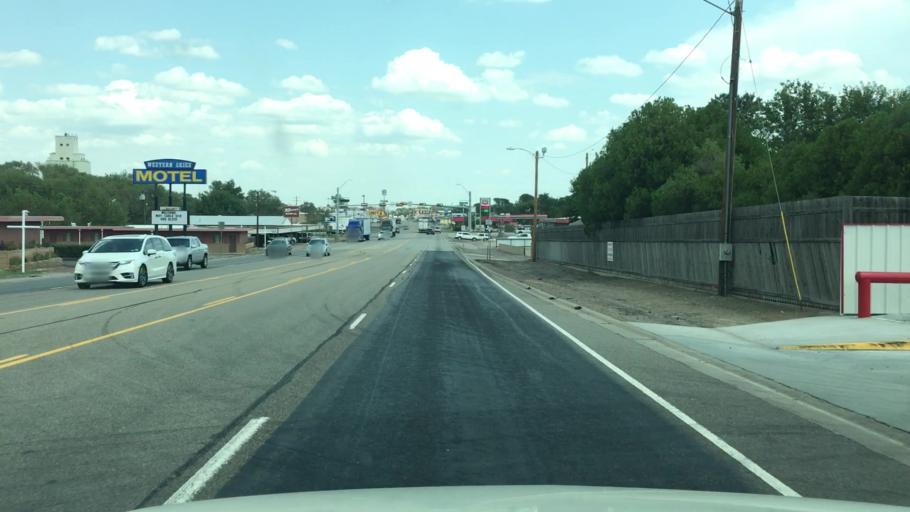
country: US
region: Texas
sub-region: Donley County
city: Clarendon
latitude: 34.9418
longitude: -100.8961
